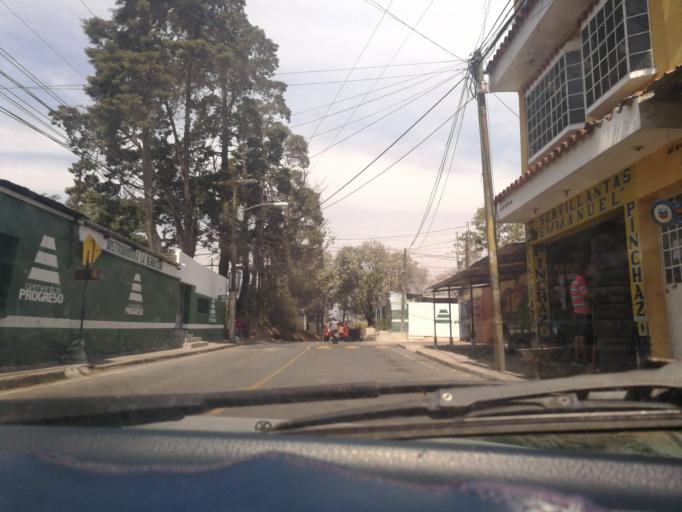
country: GT
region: Guatemala
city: Guatemala City
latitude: 14.6231
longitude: -90.4804
